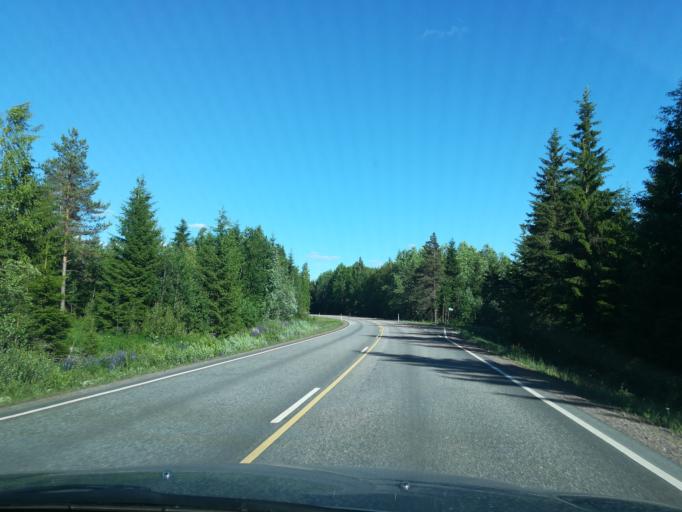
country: FI
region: South Karelia
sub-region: Imatra
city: Ruokolahti
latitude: 61.3517
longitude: 28.7346
